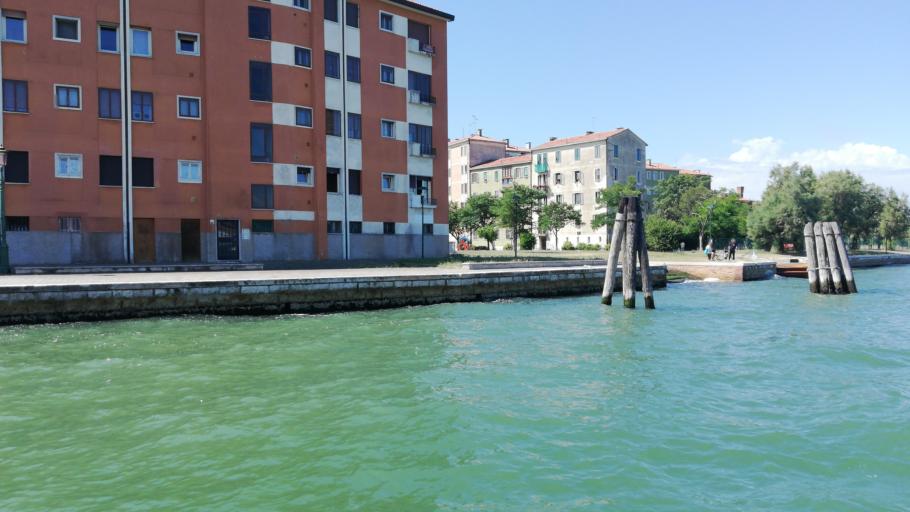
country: IT
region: Veneto
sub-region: Provincia di Venezia
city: Giudecca
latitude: 45.4292
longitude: 12.3148
